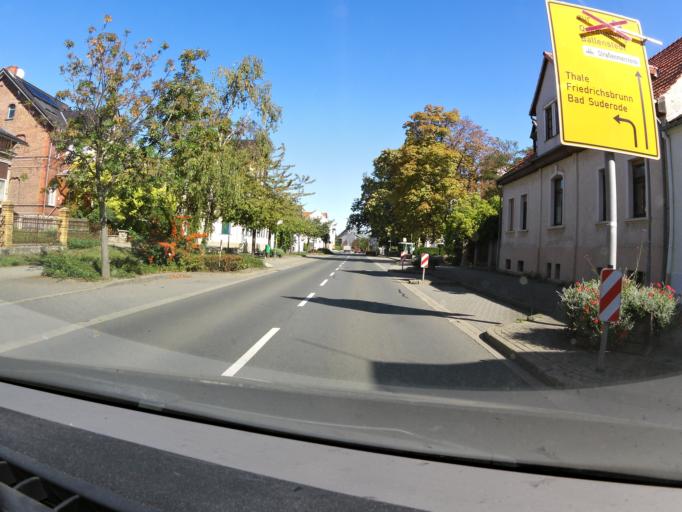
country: DE
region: Saxony-Anhalt
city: Gernrode
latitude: 51.7256
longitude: 11.1441
